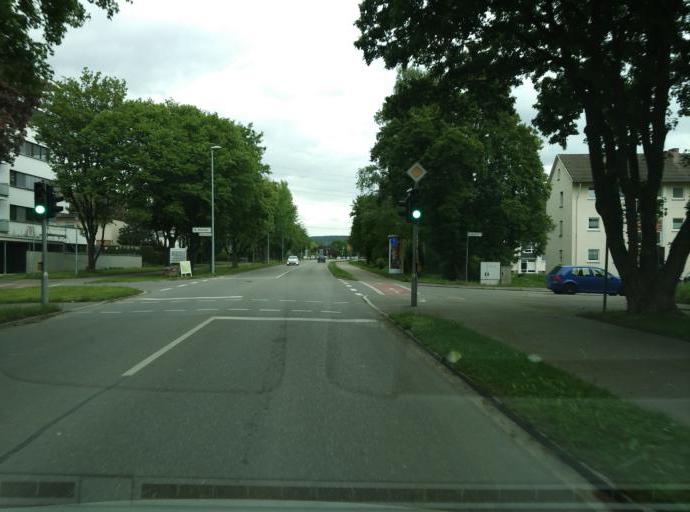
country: DE
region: Baden-Wuerttemberg
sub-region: Regierungsbezirk Stuttgart
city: Nurtingen
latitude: 48.6119
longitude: 9.3491
